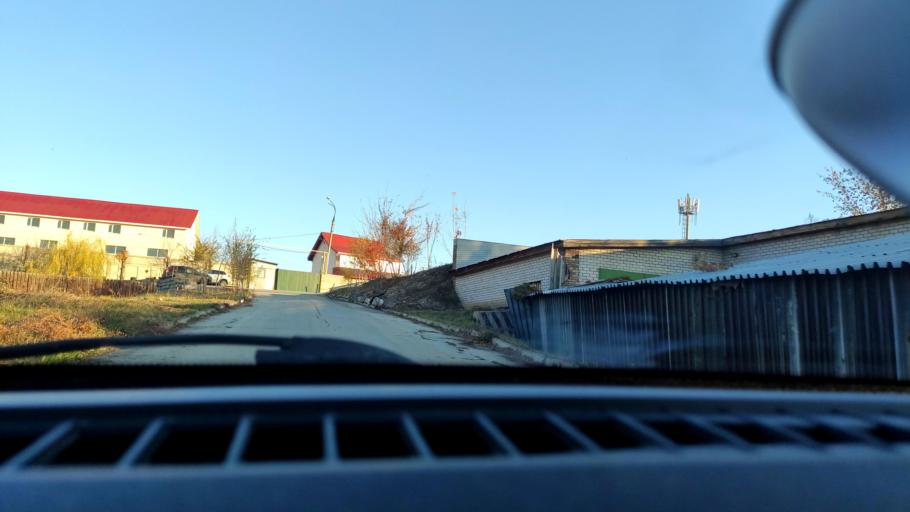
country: RU
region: Samara
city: Samara
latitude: 53.1792
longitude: 50.1814
